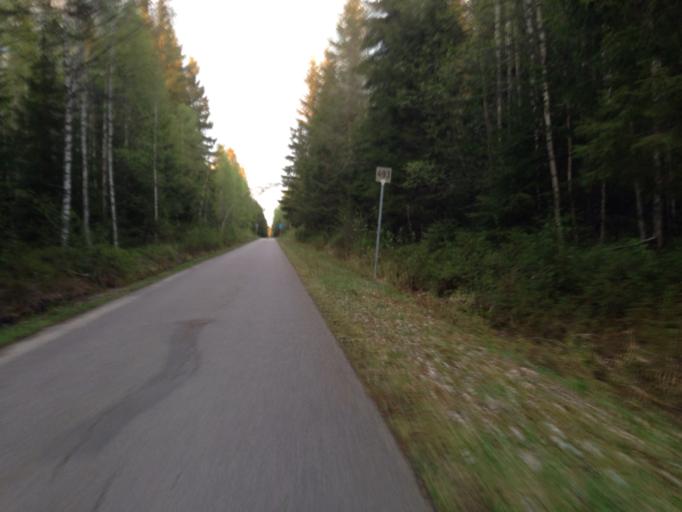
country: SE
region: Dalarna
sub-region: Ludvika Kommun
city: Ludvika
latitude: 60.1404
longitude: 15.1131
